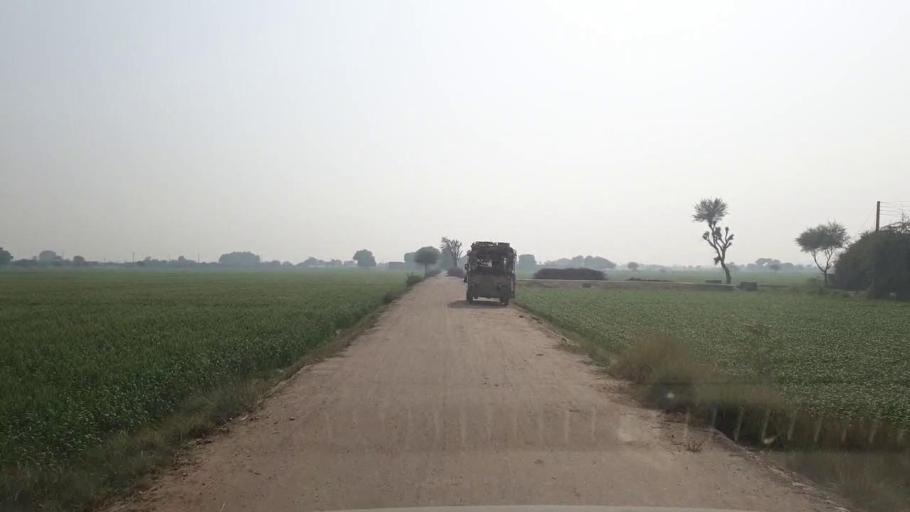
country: PK
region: Sindh
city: Hala
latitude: 25.8111
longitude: 68.4048
